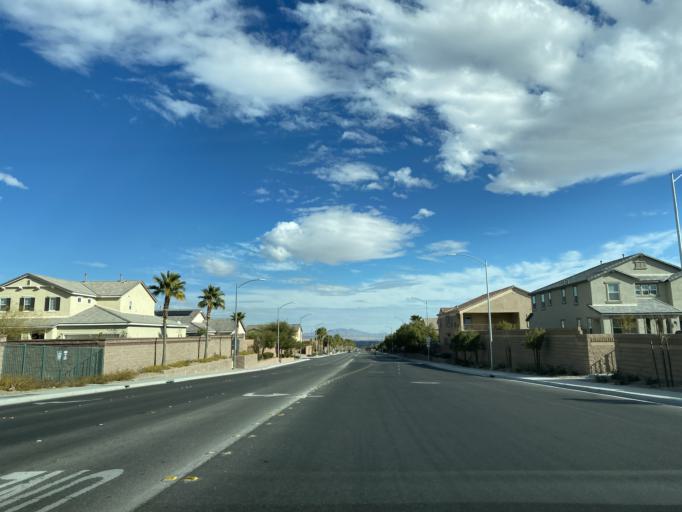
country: US
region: Nevada
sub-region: Clark County
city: Summerlin South
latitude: 36.2846
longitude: -115.3056
